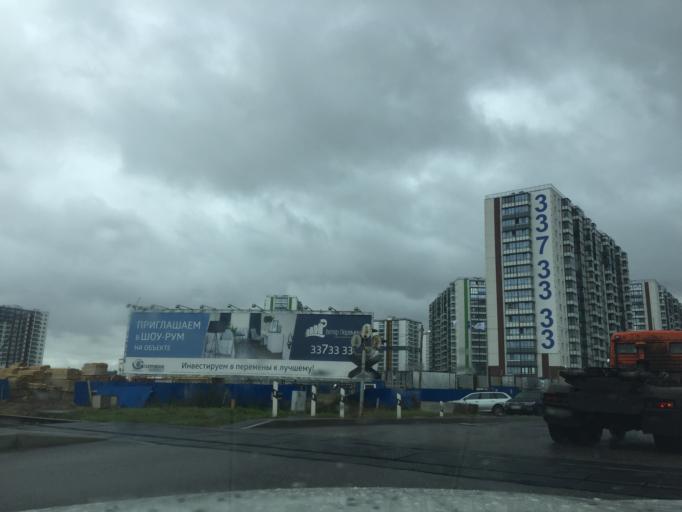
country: RU
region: St.-Petersburg
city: Uritsk
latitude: 59.7949
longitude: 30.1677
